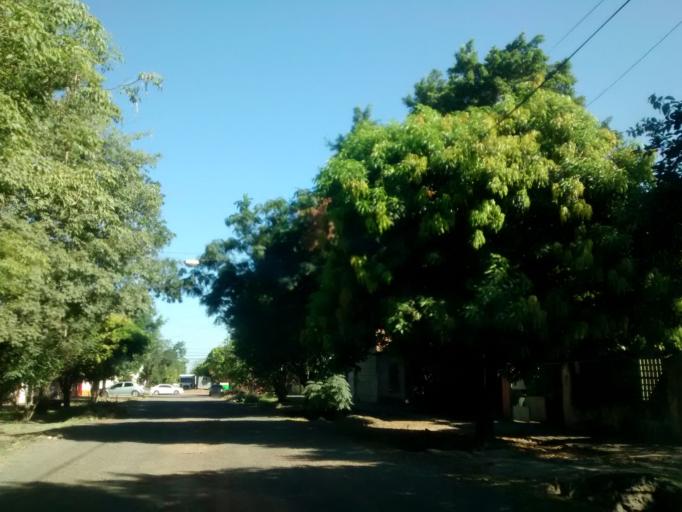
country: AR
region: Chaco
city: Resistencia
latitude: -27.4465
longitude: -59.0022
